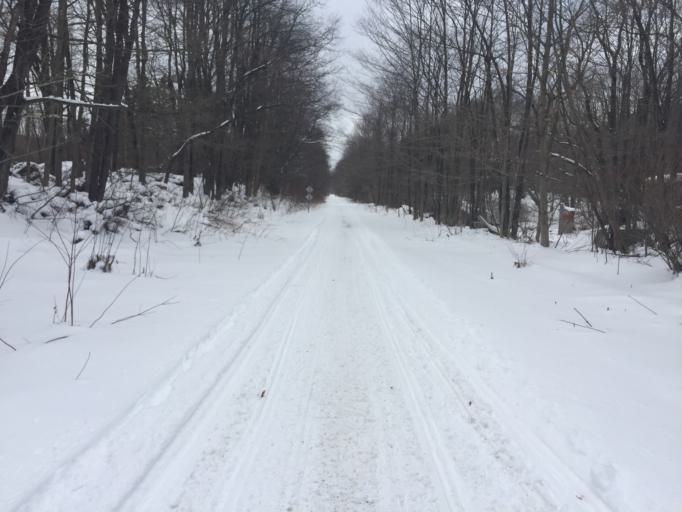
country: US
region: New York
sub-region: Cattaraugus County
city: Little Valley
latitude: 42.2521
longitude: -78.7980
